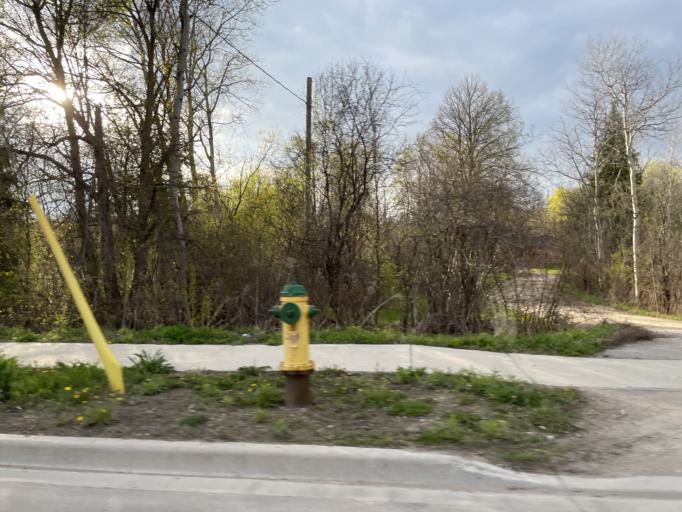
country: CA
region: Ontario
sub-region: Wellington County
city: Guelph
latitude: 43.5355
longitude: -80.2130
